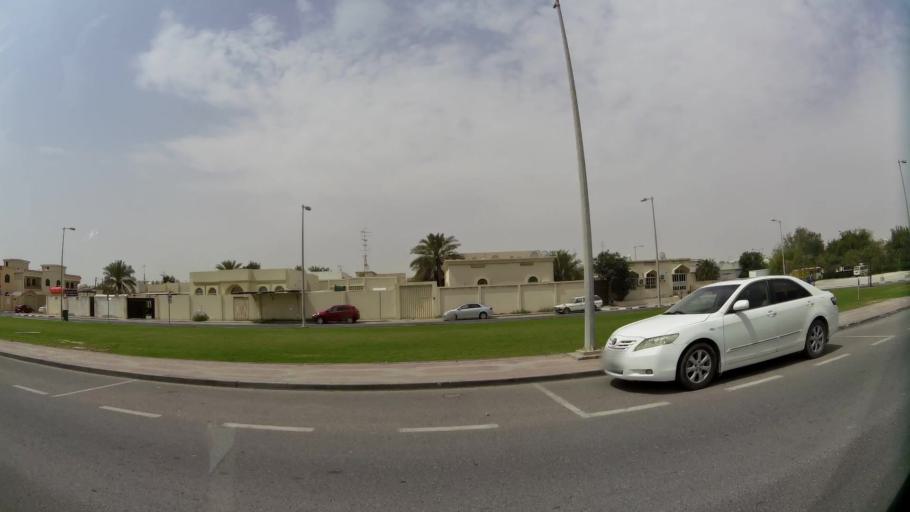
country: QA
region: Baladiyat ad Dawhah
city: Doha
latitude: 25.3132
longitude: 51.4788
